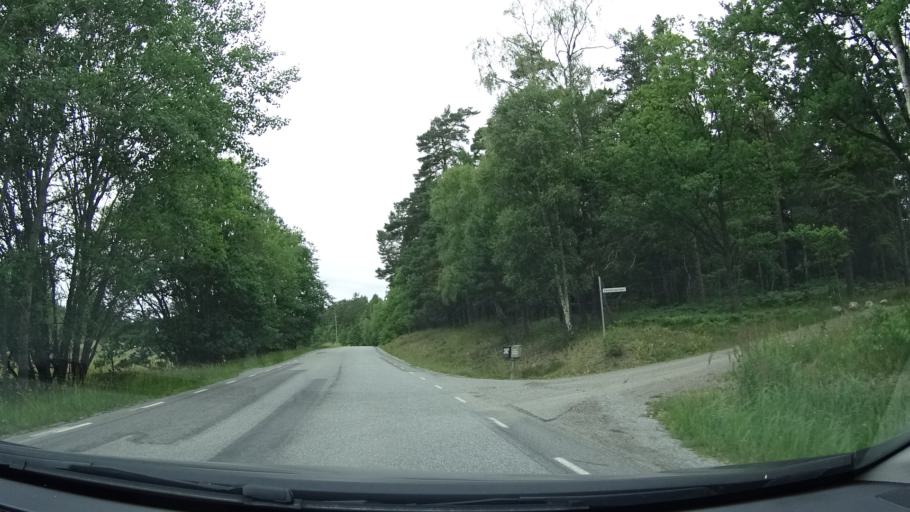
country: SE
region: Stockholm
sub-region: Varmdo Kommun
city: Hemmesta
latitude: 59.3591
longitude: 18.4875
